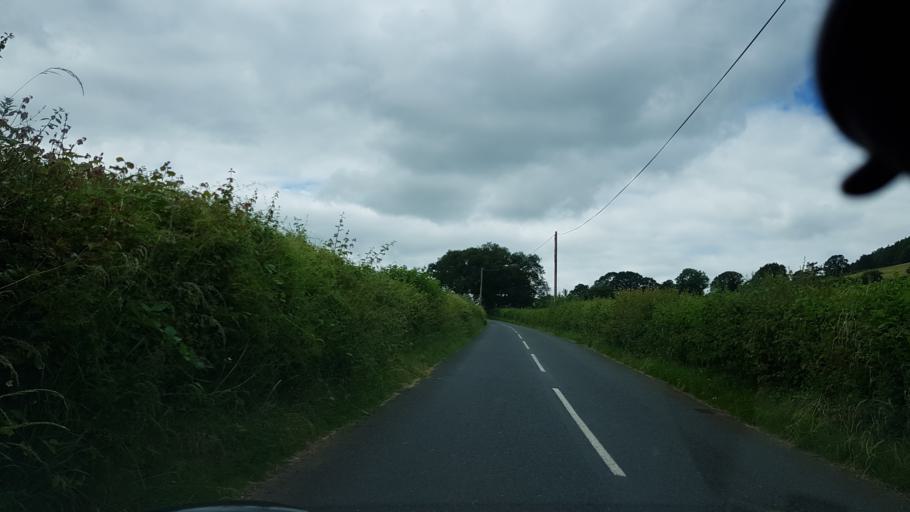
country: GB
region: England
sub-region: Herefordshire
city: Llanrothal
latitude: 51.8779
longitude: -2.8096
